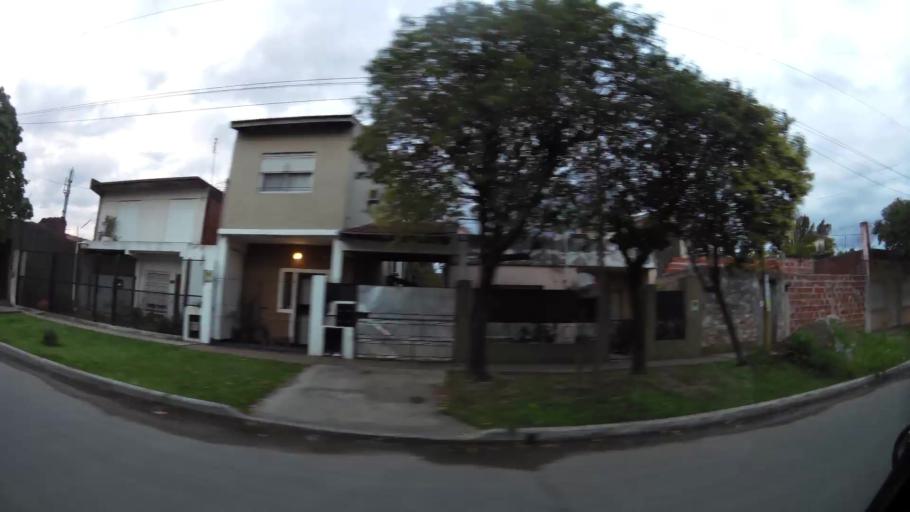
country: AR
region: Buenos Aires
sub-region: Partido de Quilmes
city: Quilmes
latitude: -34.7475
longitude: -58.2466
